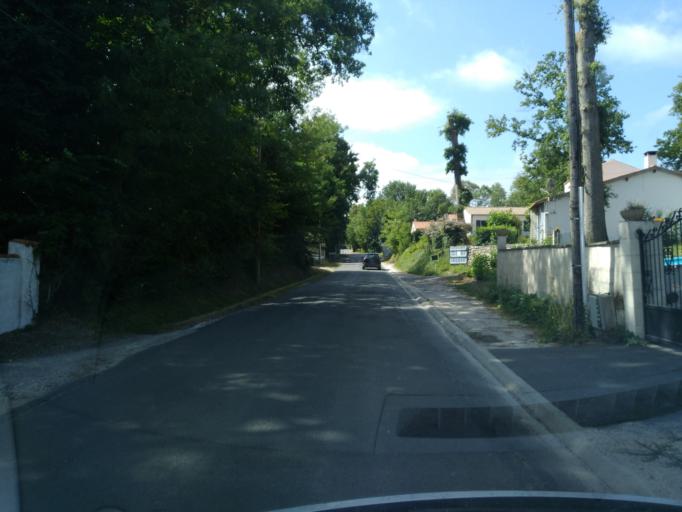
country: FR
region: Poitou-Charentes
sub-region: Departement de la Charente-Maritime
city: Breuillet
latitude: 45.6931
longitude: -1.0695
